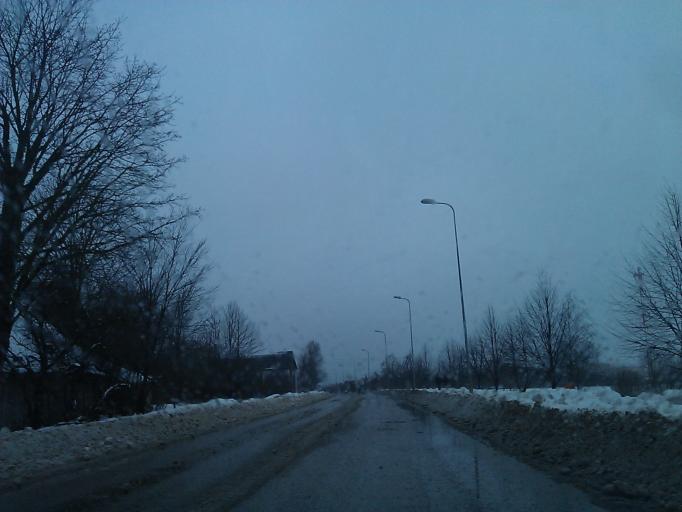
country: LV
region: Cesu Rajons
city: Cesis
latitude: 57.3005
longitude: 25.2969
